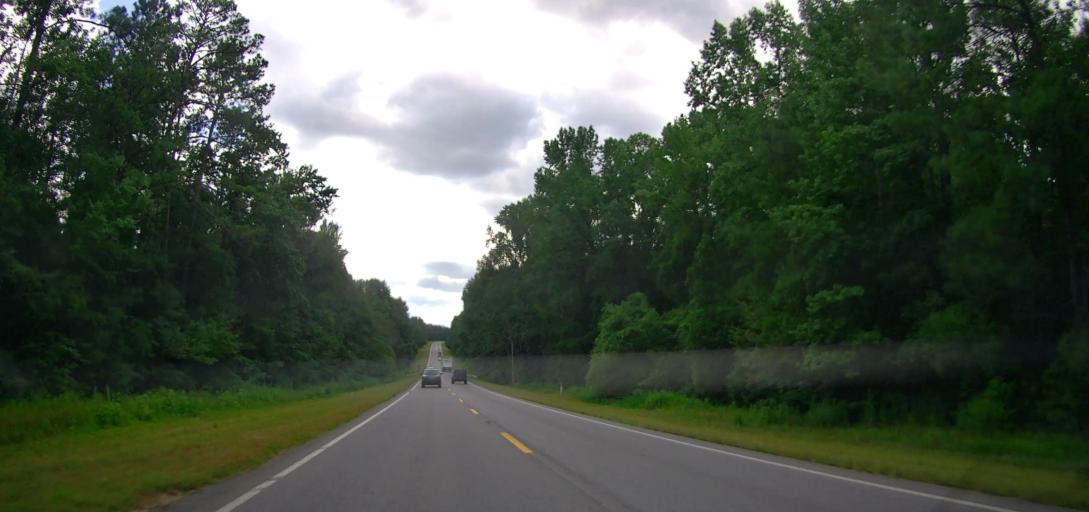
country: US
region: Alabama
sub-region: Russell County
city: Ladonia
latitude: 32.4526
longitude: -85.2106
